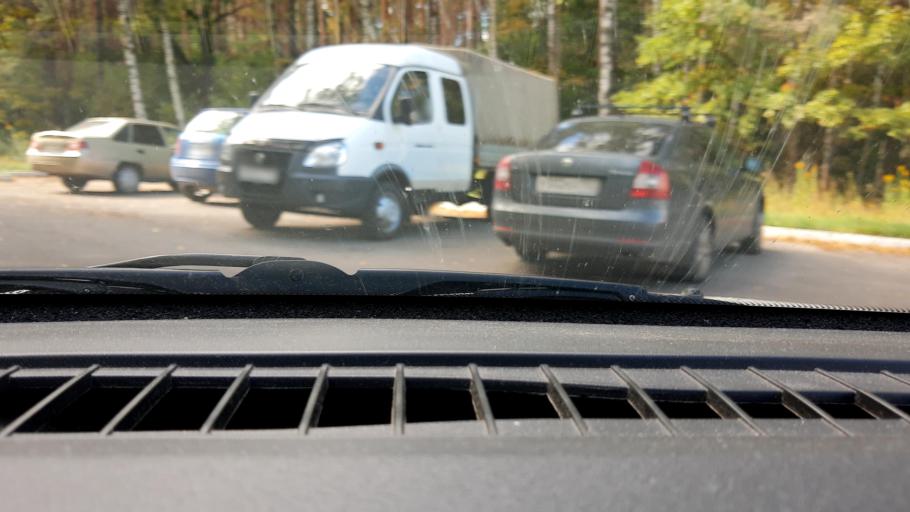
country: RU
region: Nizjnij Novgorod
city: Afonino
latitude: 56.1850
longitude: 44.1080
